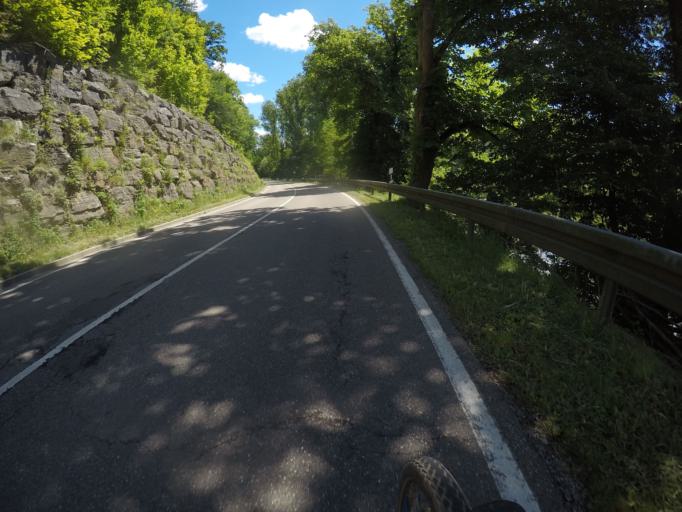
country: DE
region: Baden-Wuerttemberg
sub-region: Tuebingen Region
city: Hirrlingen
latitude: 48.4462
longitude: 8.8188
